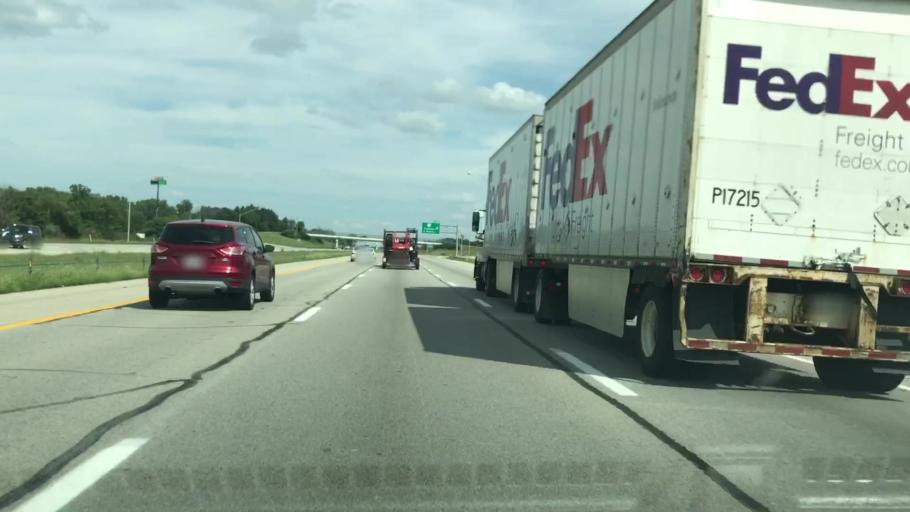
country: US
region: Ohio
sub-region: Clark County
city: Lisbon
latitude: 39.9330
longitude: -83.6186
